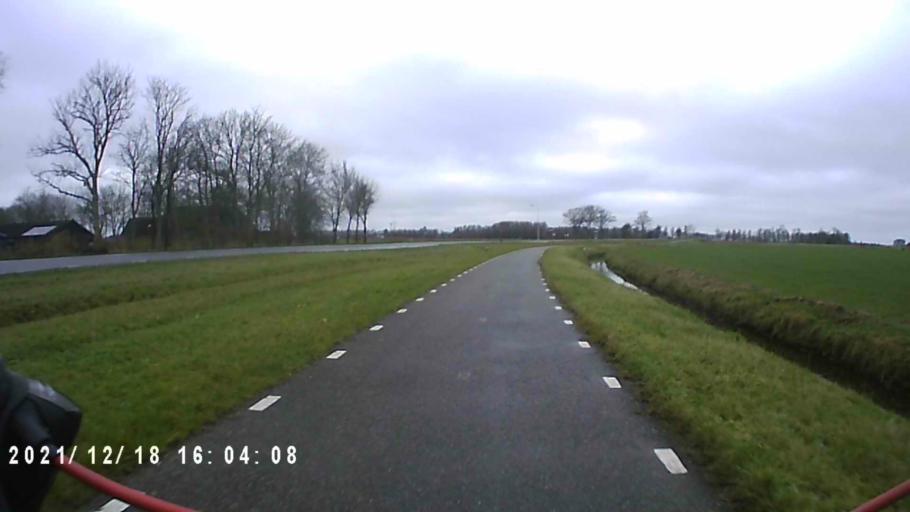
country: NL
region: Friesland
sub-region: Gemeente Dongeradeel
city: Anjum
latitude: 53.3512
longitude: 6.0786
